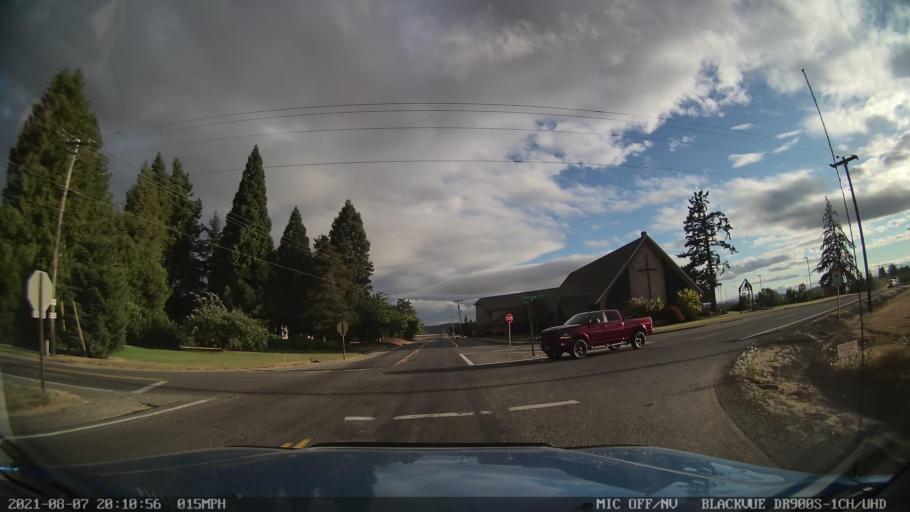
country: US
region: Oregon
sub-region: Marion County
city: Hayesville
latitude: 44.9585
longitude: -122.8856
